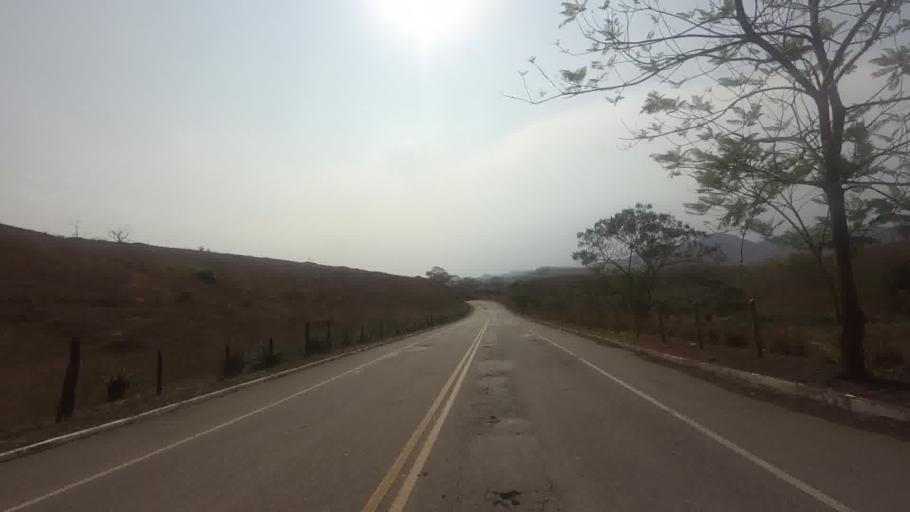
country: BR
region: Rio de Janeiro
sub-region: Bom Jesus Do Itabapoana
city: Bom Jesus do Itabapoana
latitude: -21.1384
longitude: -41.6333
